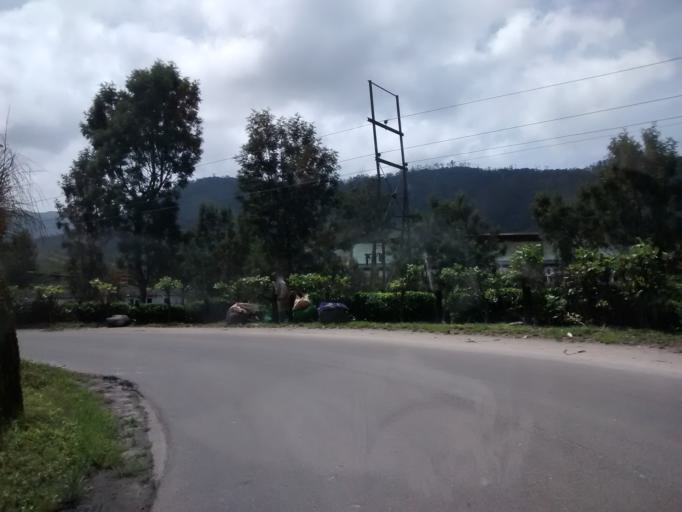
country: IN
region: Kerala
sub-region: Idukki
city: Munnar
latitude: 10.1051
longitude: 77.1179
